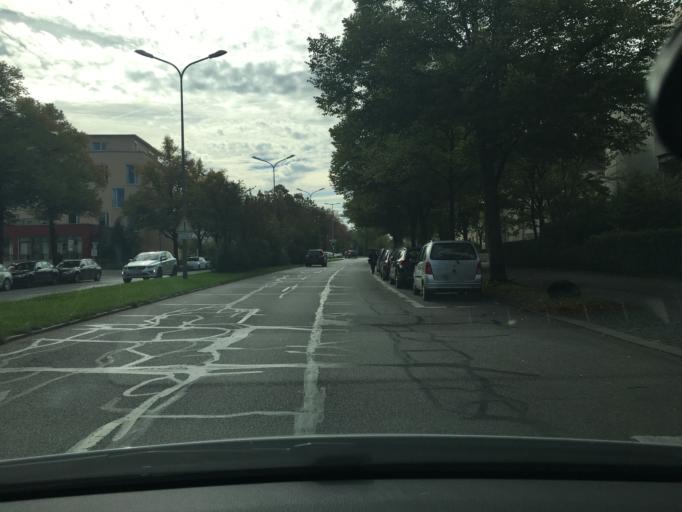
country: DE
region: Bavaria
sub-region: Upper Bavaria
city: Pullach im Isartal
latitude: 48.1035
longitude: 11.5243
